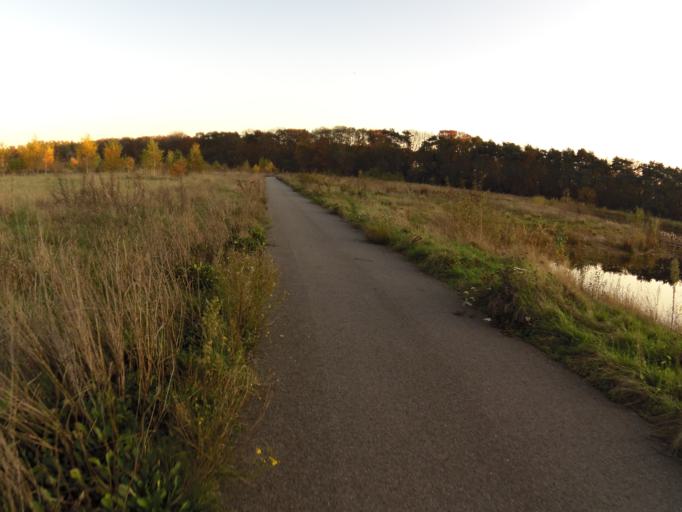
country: NL
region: North Brabant
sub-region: Gemeente Haaren
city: Haaren
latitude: 51.6713
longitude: 5.1906
